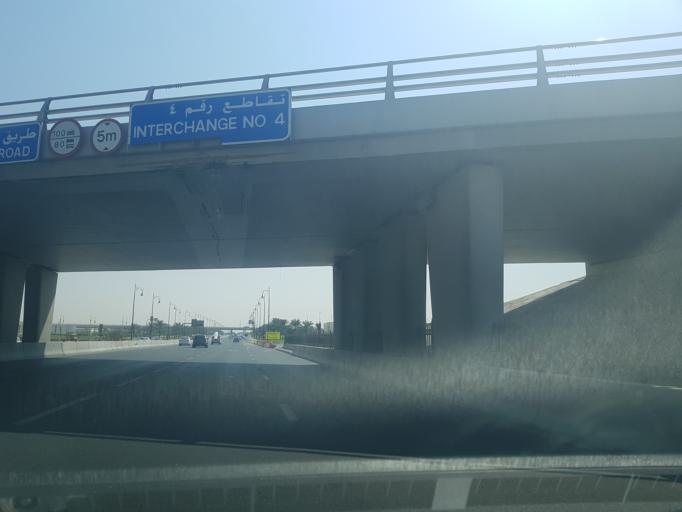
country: AE
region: Ash Shariqah
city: Sharjah
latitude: 25.3178
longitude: 55.5177
